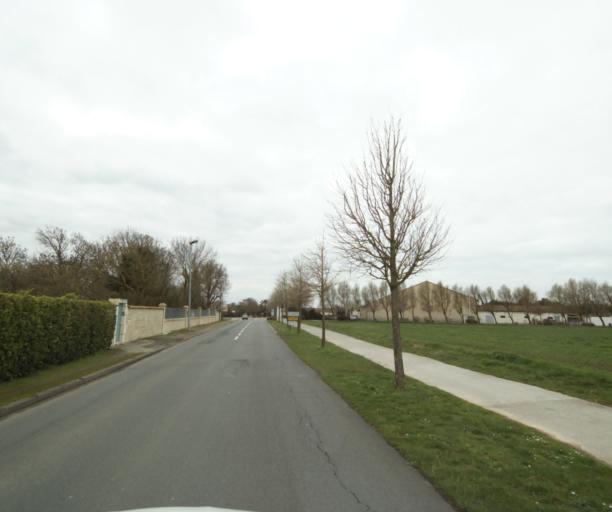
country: FR
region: Poitou-Charentes
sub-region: Departement de la Charente-Maritime
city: Lagord
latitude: 46.1952
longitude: -1.1568
